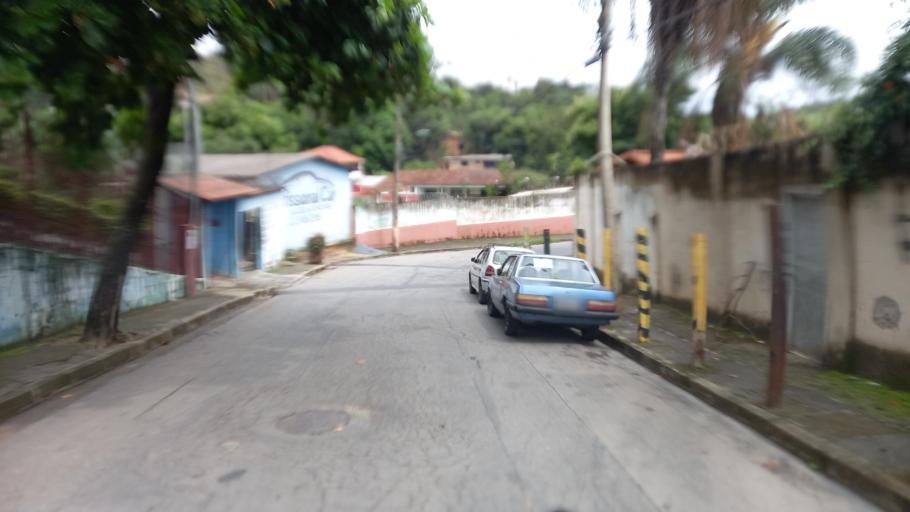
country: BR
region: Minas Gerais
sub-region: Belo Horizonte
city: Belo Horizonte
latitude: -19.9067
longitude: -43.8818
